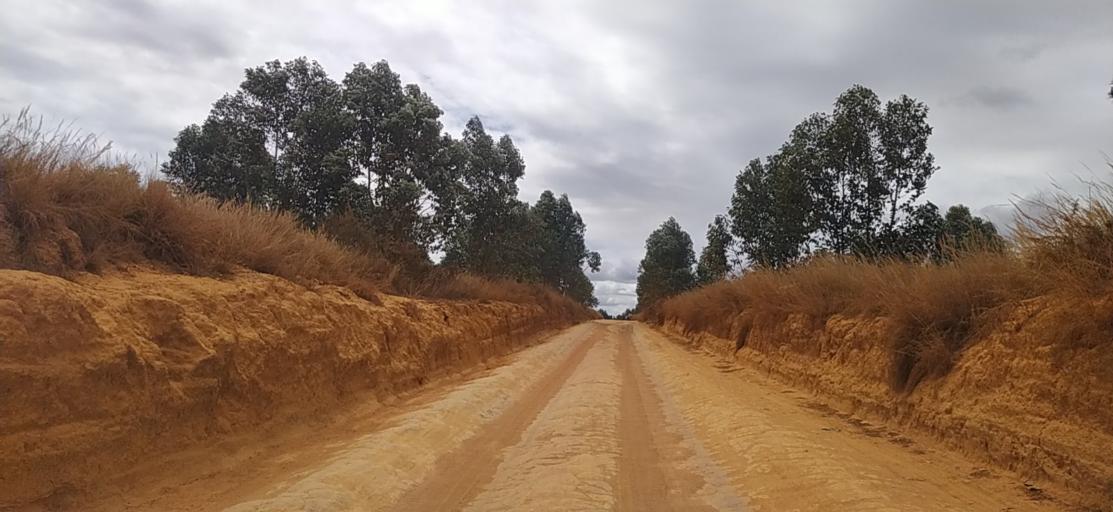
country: MG
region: Alaotra Mangoro
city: Ambatondrazaka
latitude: -17.9948
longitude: 48.2662
